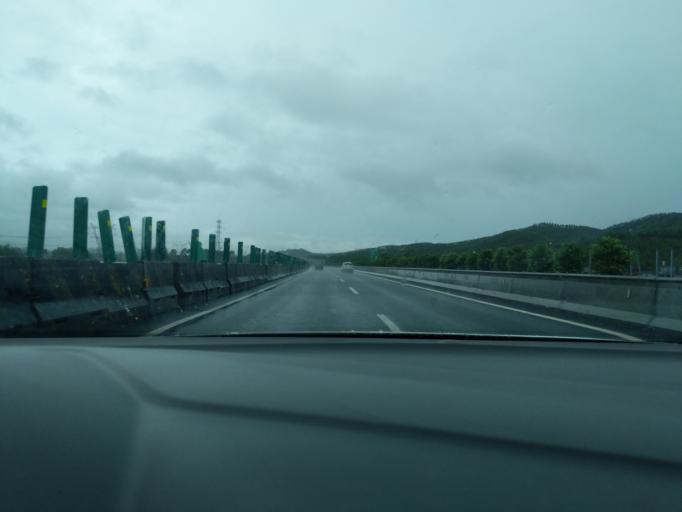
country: CN
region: Guangdong
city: Liangxi
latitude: 22.2706
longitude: 112.3274
